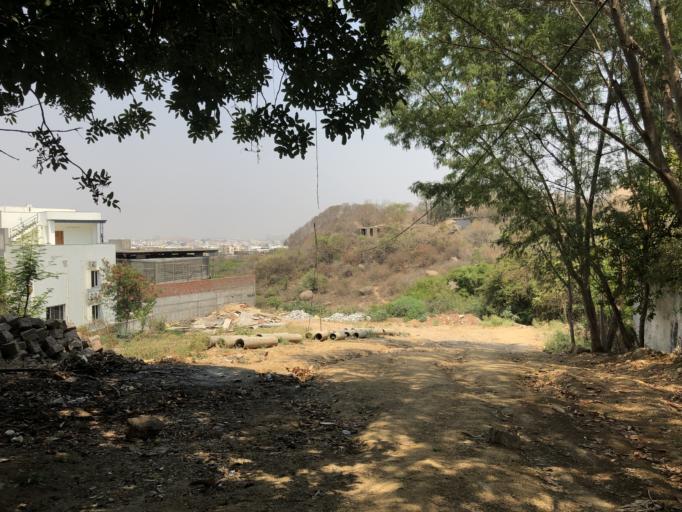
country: IN
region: Telangana
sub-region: Rangareddi
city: Kukatpalli
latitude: 17.4401
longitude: 78.4055
